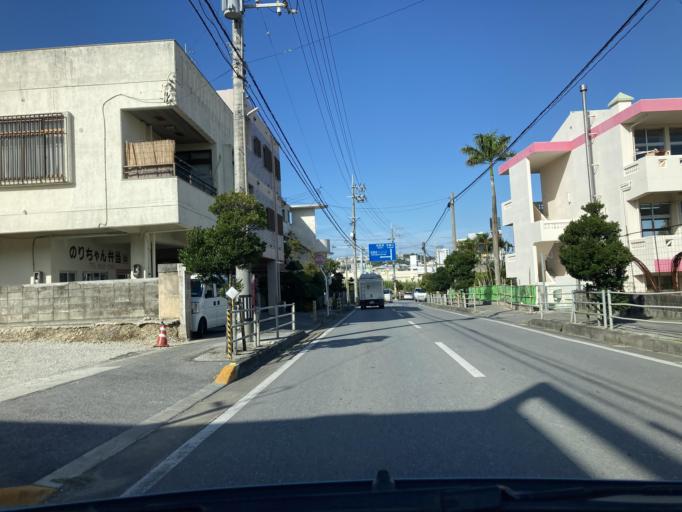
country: JP
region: Okinawa
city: Tomigusuku
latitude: 26.1843
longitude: 127.7072
